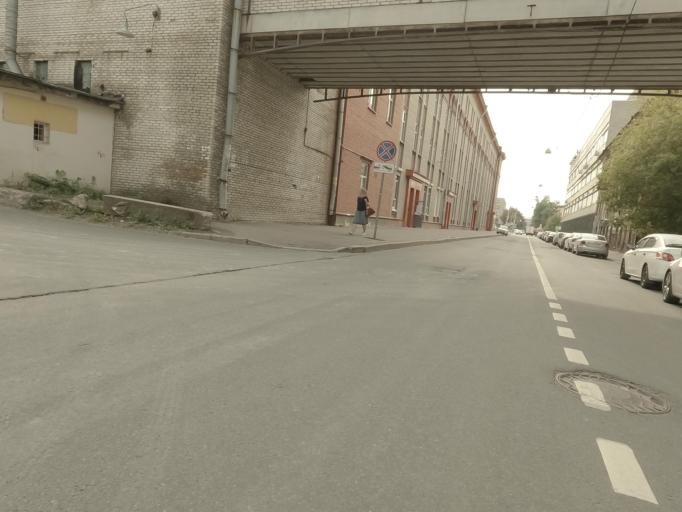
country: RU
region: St.-Petersburg
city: Admiralteisky
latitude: 59.8978
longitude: 30.2920
